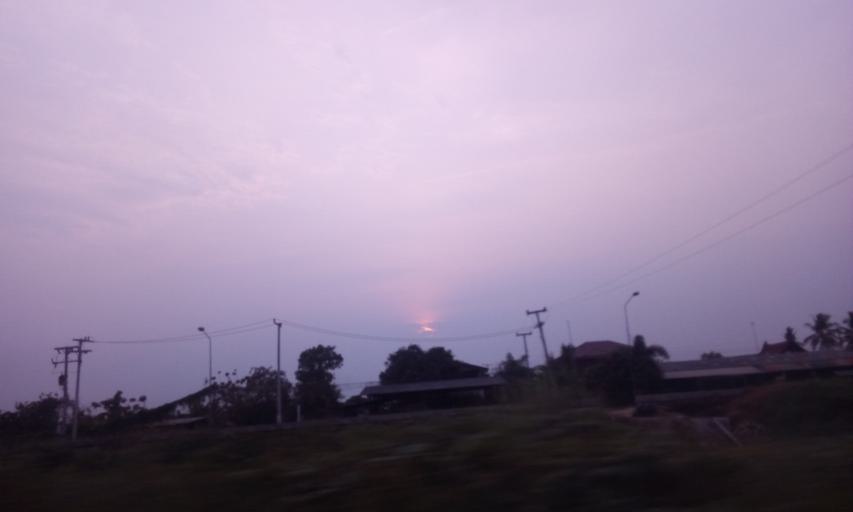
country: TH
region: Pathum Thani
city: Nong Suea
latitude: 14.0400
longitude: 100.8936
